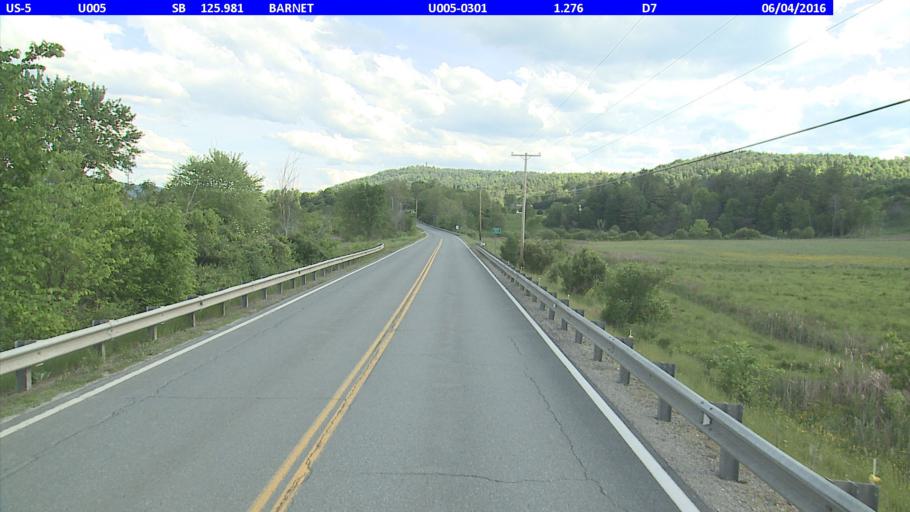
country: US
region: New Hampshire
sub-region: Grafton County
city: Woodsville
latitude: 44.2735
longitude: -72.0693
